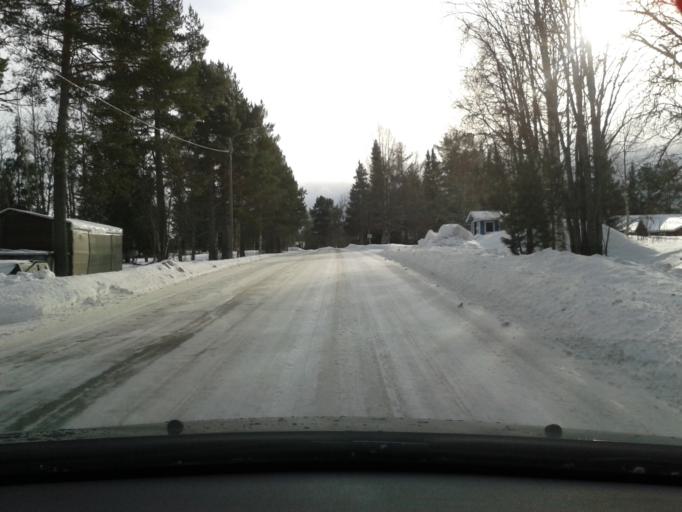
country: SE
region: Vaesterbotten
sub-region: Vilhelmina Kommun
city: Sjoberg
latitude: 64.6926
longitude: 16.2672
